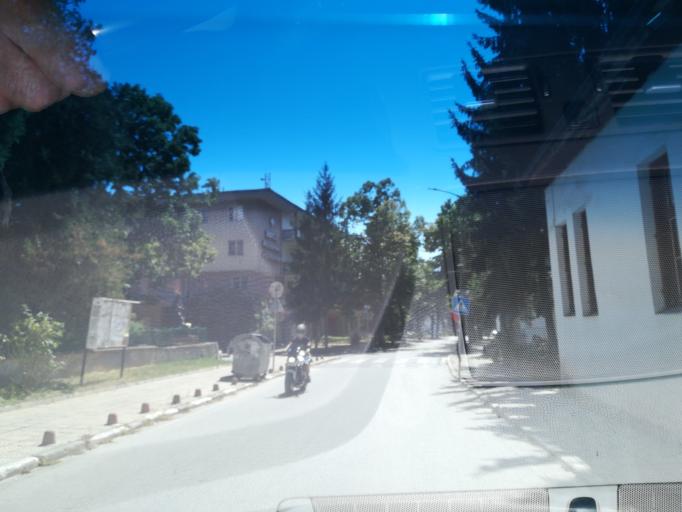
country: BG
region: Pazardzhik
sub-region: Obshtina Strelcha
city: Strelcha
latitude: 42.5073
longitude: 24.3207
